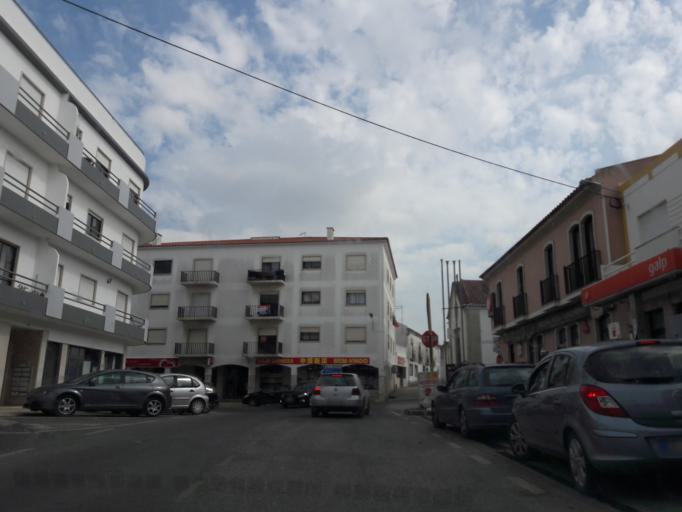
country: PT
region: Leiria
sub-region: Peniche
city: Atouguia da Baleia
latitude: 39.3401
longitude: -9.3271
